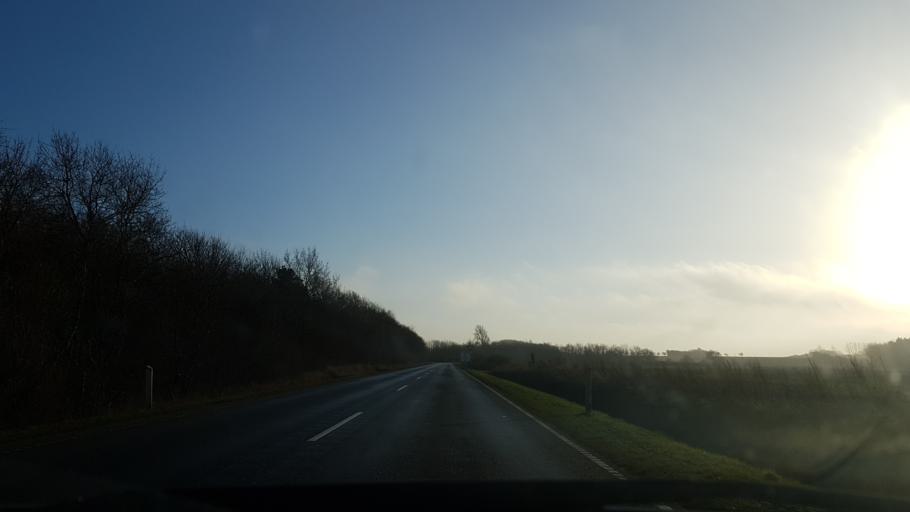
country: DK
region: South Denmark
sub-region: Haderslev Kommune
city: Vojens
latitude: 55.2018
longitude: 9.1944
